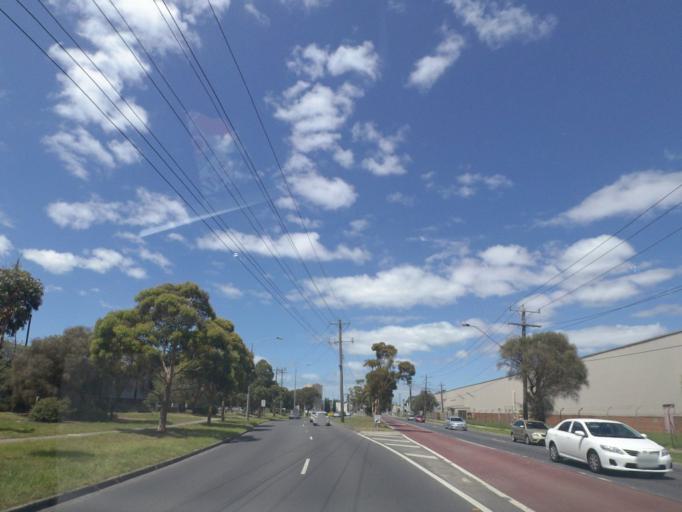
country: AU
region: Victoria
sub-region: Brimbank
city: Sunshine North
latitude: -37.7776
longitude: 144.8287
